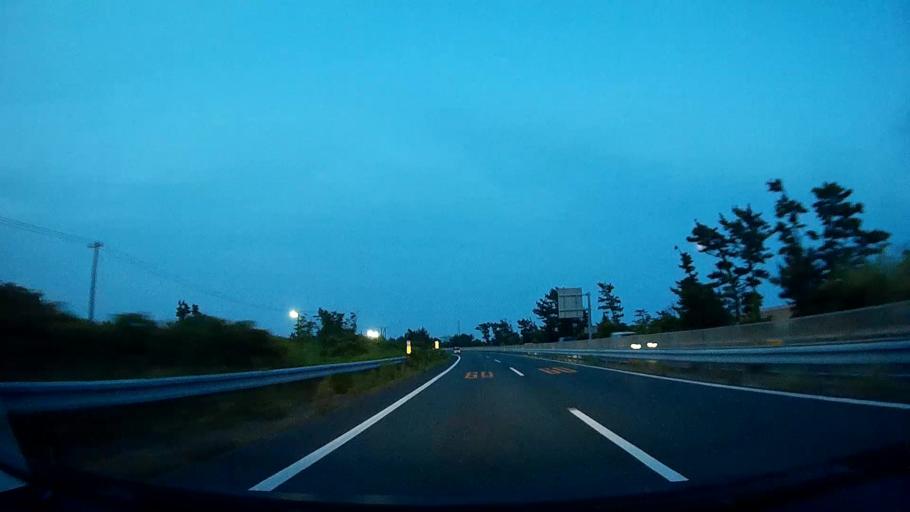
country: JP
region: Shizuoka
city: Hamamatsu
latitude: 34.6753
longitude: 137.6543
